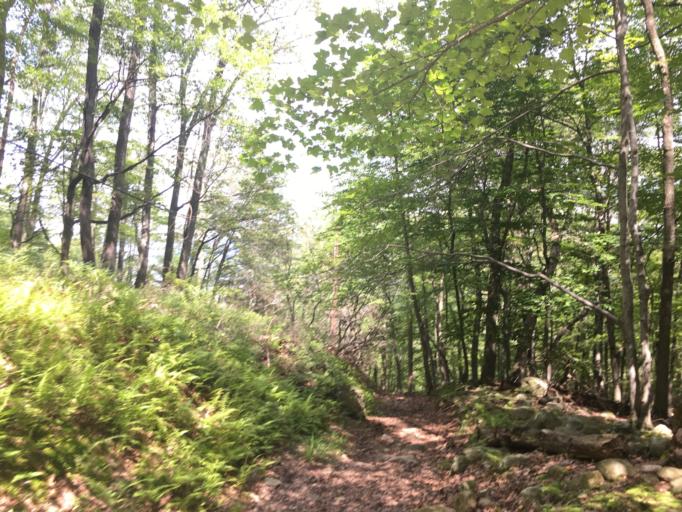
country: US
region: New York
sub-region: Orange County
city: Fort Montgomery
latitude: 41.3075
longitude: -73.9944
